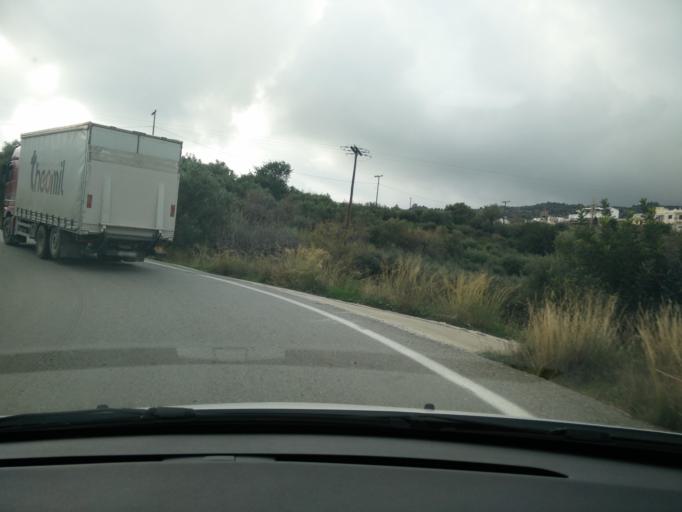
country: GR
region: Crete
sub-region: Nomos Lasithiou
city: Gra Liyia
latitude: 35.0265
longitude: 25.5684
